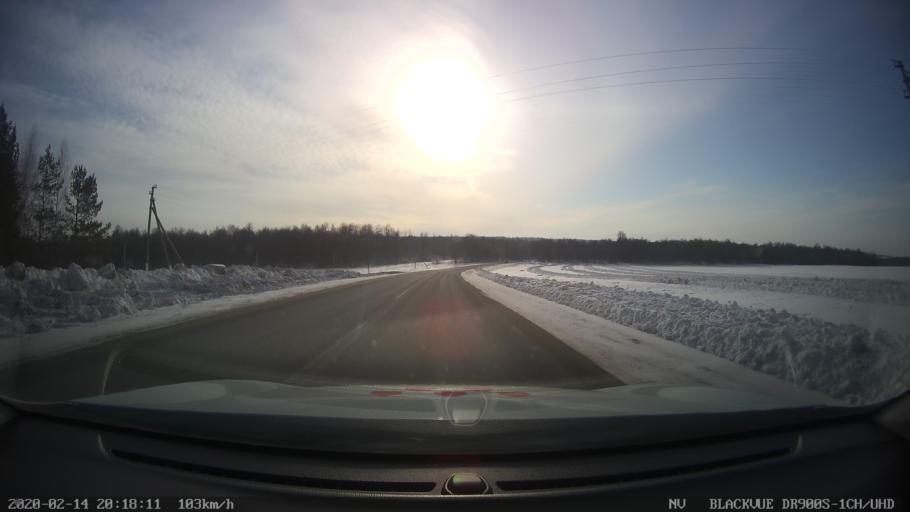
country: RU
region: Tatarstan
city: Verkhniy Uslon
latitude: 55.5897
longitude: 48.8855
